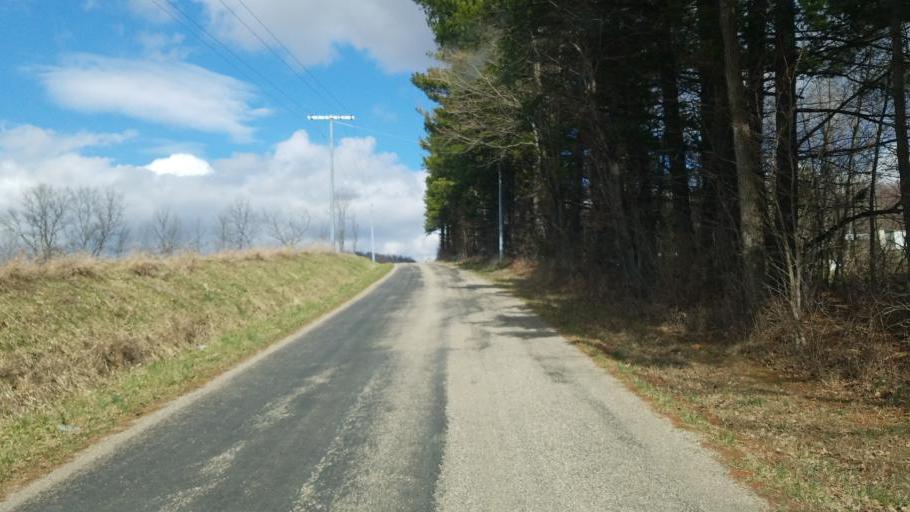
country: US
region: Ohio
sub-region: Sandusky County
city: Bellville
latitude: 40.5715
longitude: -82.4844
